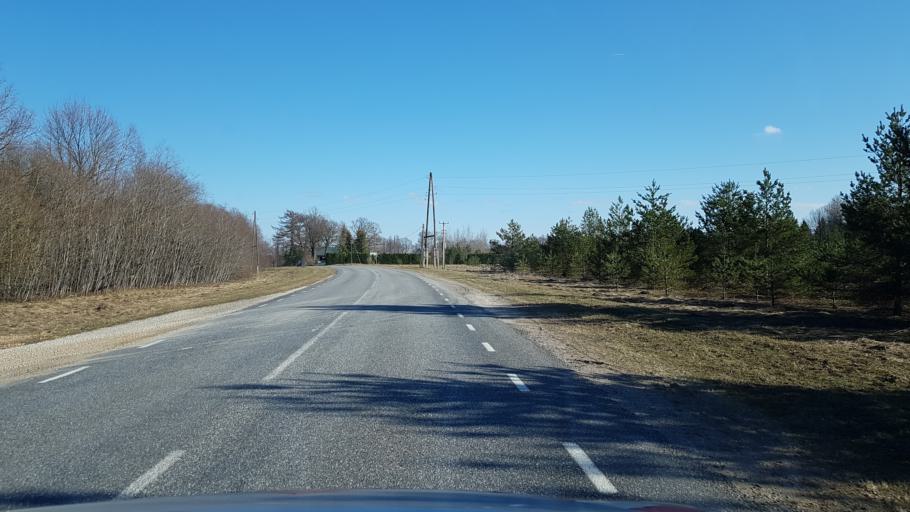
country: EE
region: Laeaene-Virumaa
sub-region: Haljala vald
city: Haljala
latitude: 59.4657
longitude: 26.1830
